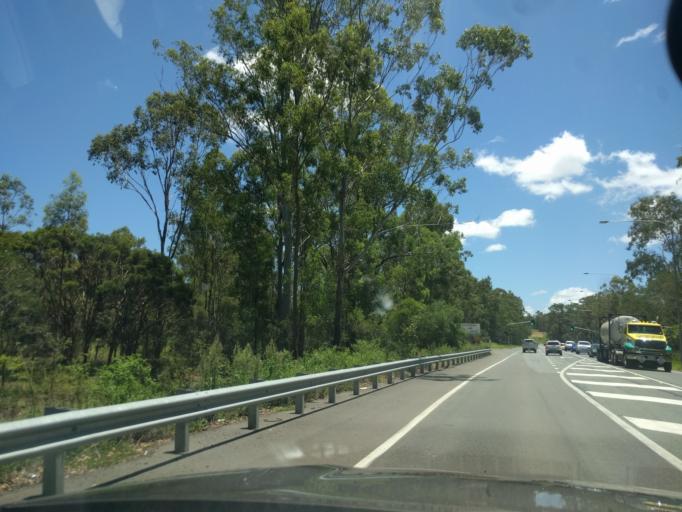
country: AU
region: Queensland
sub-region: Logan
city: Cedar Vale
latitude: -27.8454
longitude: 153.0210
